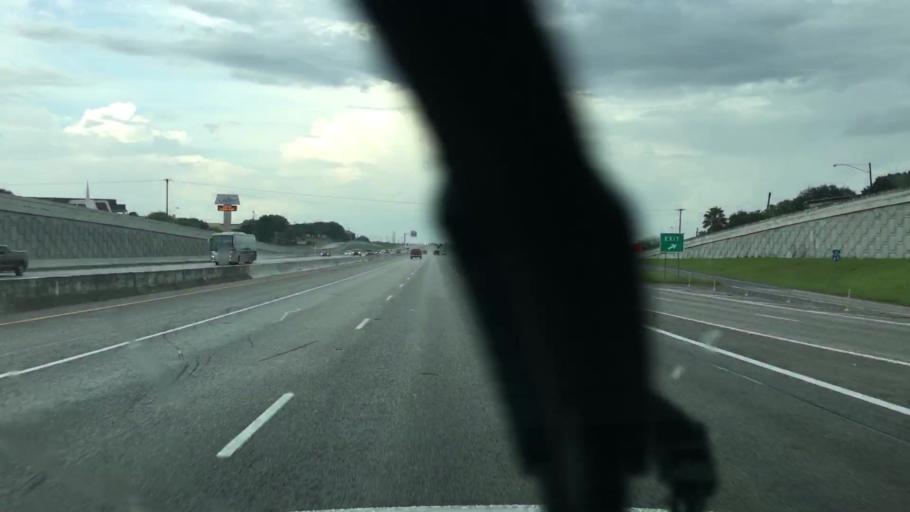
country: US
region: Texas
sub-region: Nueces County
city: Robstown
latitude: 27.8676
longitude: -97.6230
